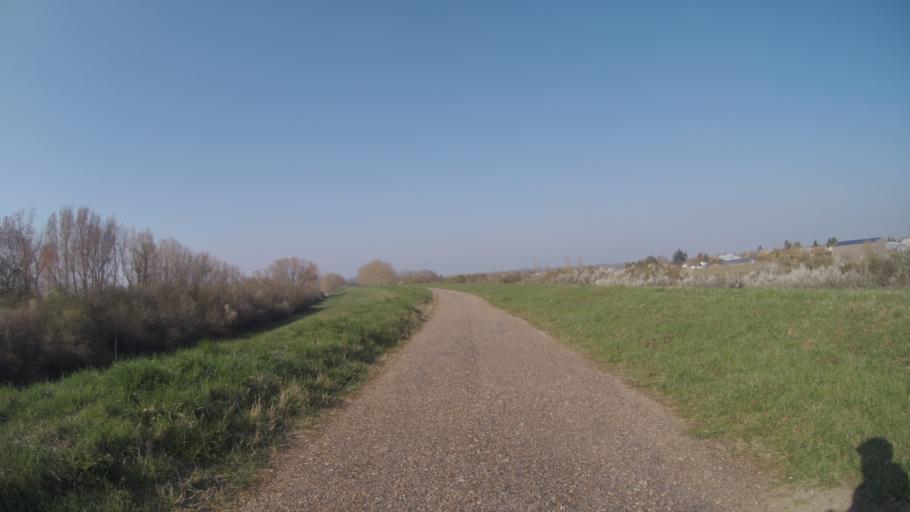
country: FR
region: Centre
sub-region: Departement du Loiret
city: Mardie
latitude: 47.8721
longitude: 2.0366
